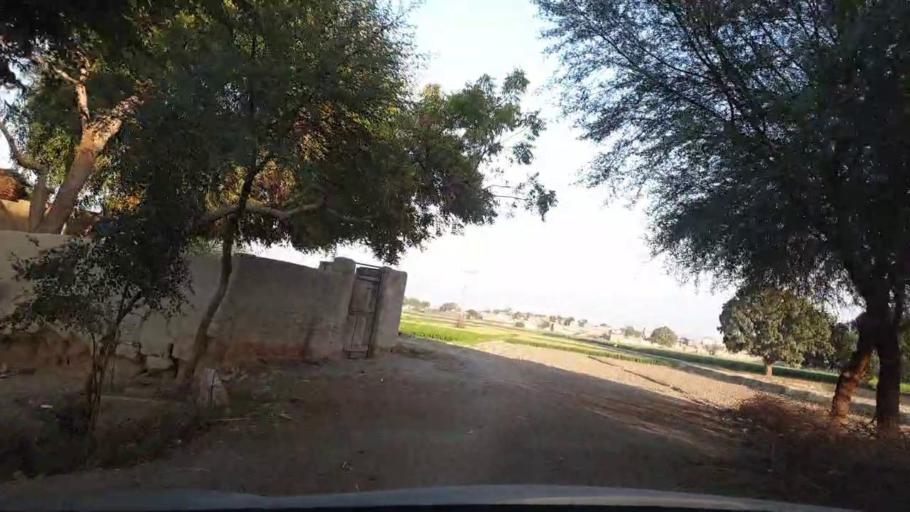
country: PK
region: Sindh
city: Tando Allahyar
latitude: 25.5557
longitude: 68.7943
